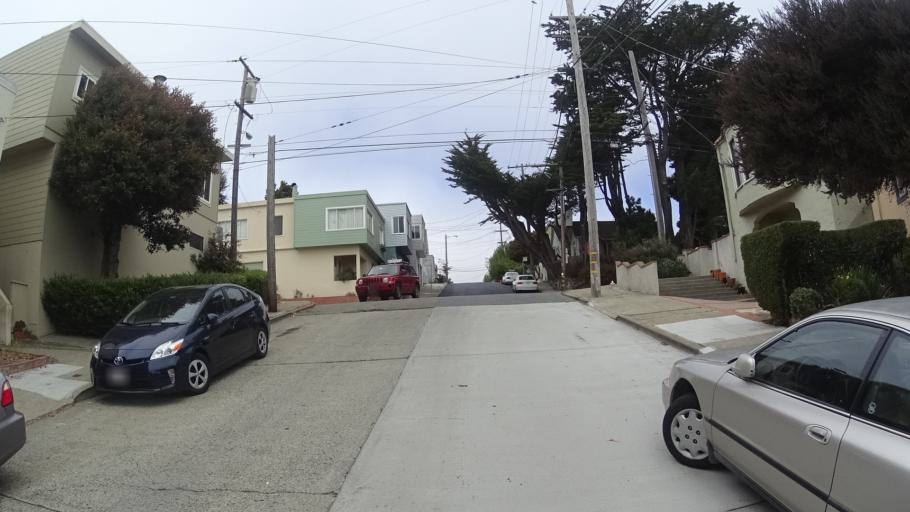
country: US
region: California
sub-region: San Mateo County
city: Daly City
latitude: 37.7329
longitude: -122.4420
